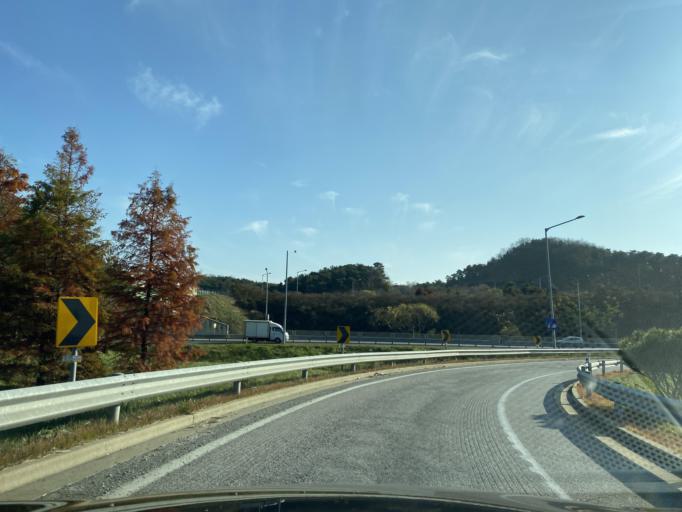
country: KR
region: Chungcheongnam-do
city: Asan
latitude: 36.7808
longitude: 126.9398
